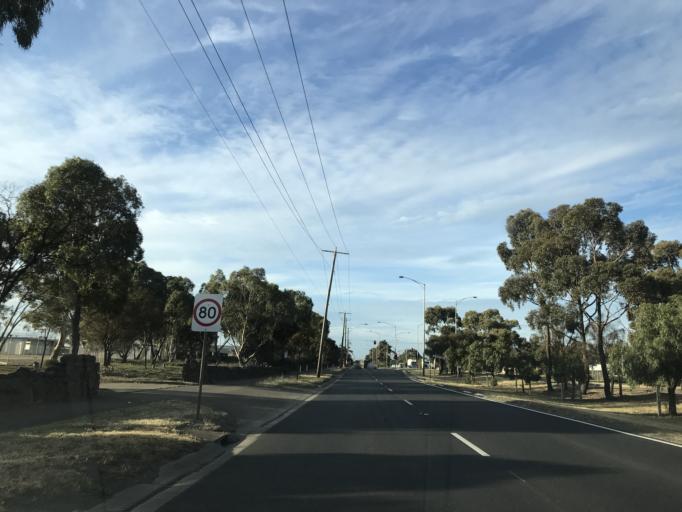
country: AU
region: Victoria
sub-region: Brimbank
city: Derrimut
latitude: -37.8224
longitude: 144.7861
